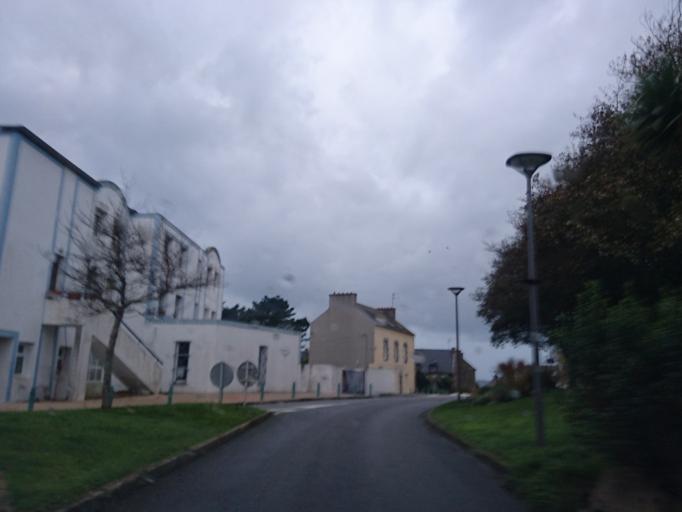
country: FR
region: Brittany
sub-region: Departement du Finistere
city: Le Conquet
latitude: 48.3594
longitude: -4.7713
